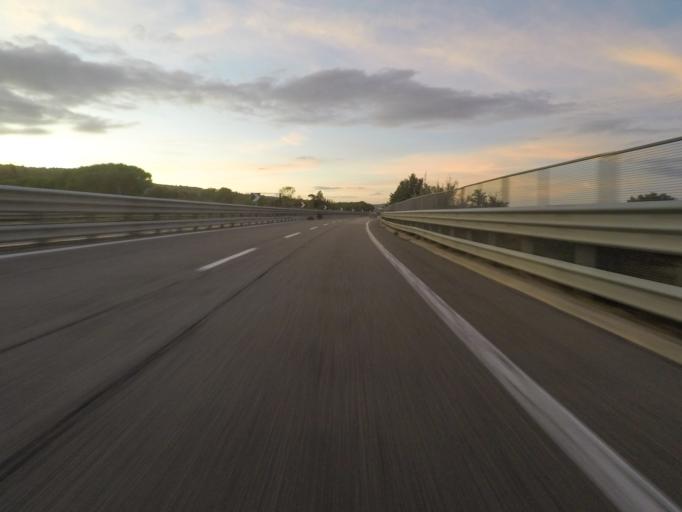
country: IT
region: Tuscany
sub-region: Provincia di Siena
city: Sinalunga
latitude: 43.2304
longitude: 11.7314
